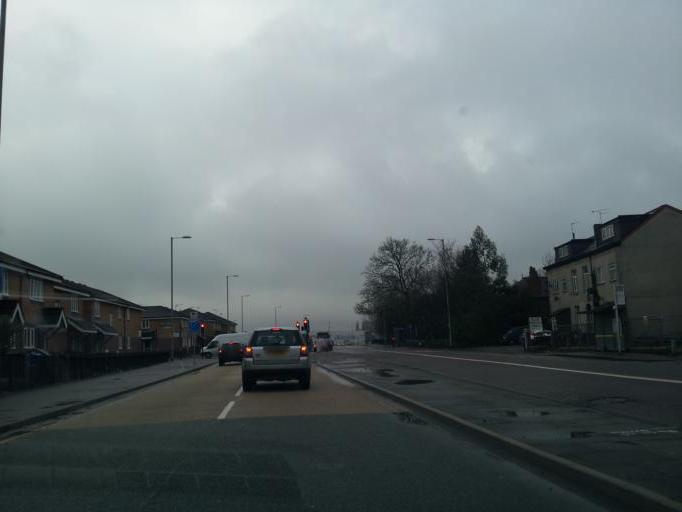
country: GB
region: England
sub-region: Manchester
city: Blackley
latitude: 53.5060
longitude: -2.2177
